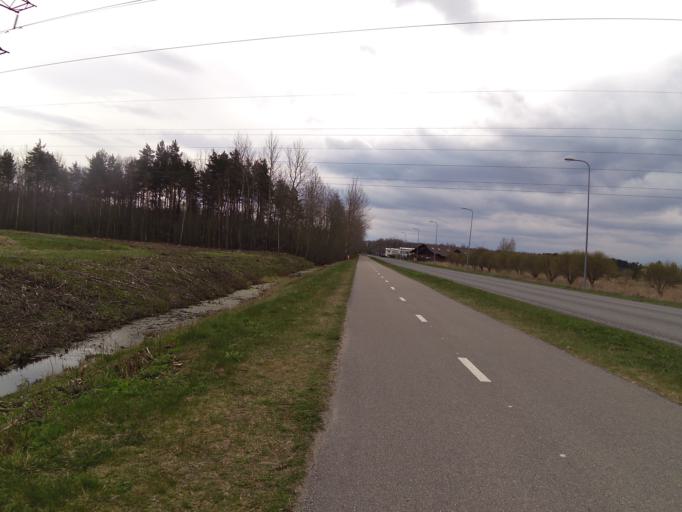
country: EE
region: Harju
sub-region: Kiili vald
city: Kiili
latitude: 59.3684
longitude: 24.8155
